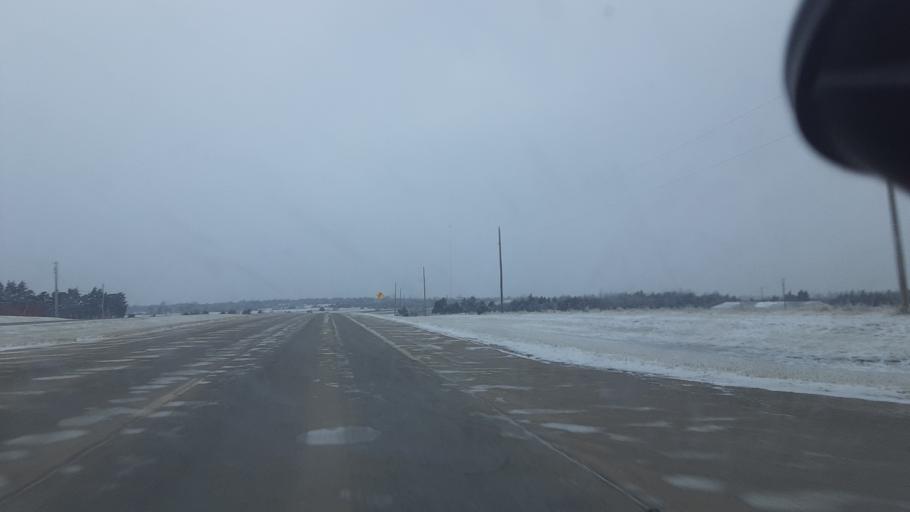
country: US
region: Oklahoma
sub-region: Logan County
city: Langston
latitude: 35.9077
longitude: -97.3363
